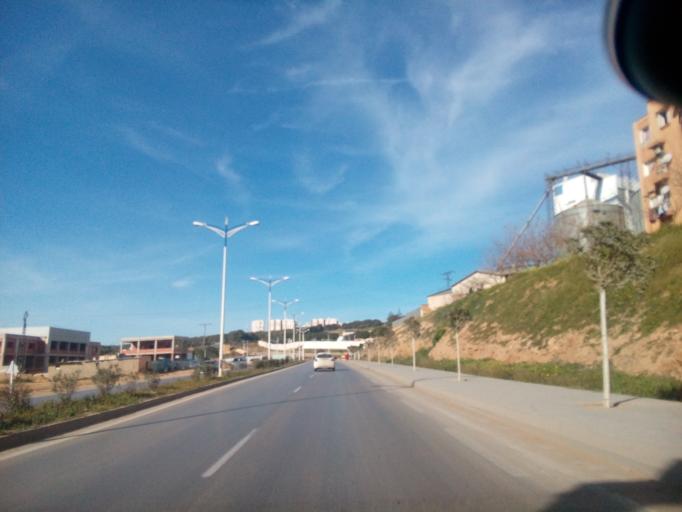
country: DZ
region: Mostaganem
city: Mostaganem
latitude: 35.9399
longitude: 0.1158
